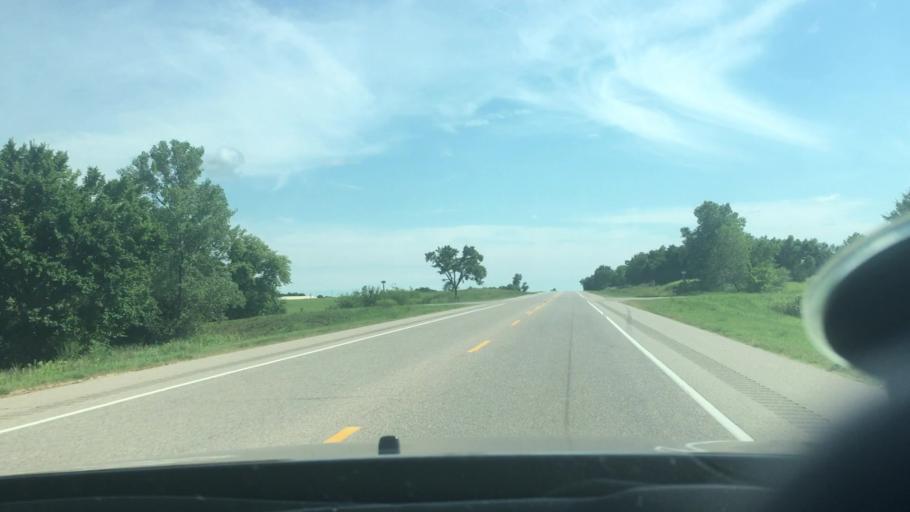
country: US
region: Oklahoma
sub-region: Seminole County
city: Seminole
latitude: 35.1604
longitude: -96.6745
